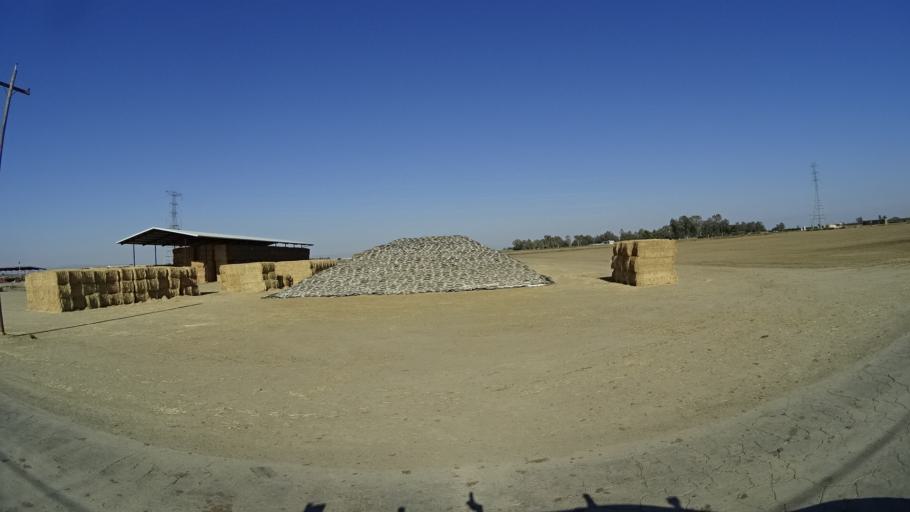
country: US
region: California
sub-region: Fresno County
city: Riverdale
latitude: 36.3491
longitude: -119.8871
